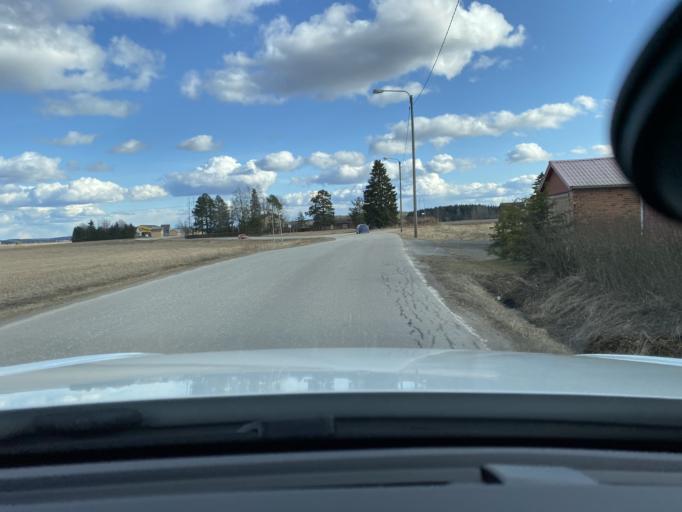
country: FI
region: Pirkanmaa
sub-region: Lounais-Pirkanmaa
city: Punkalaidun
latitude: 61.1074
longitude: 23.1071
